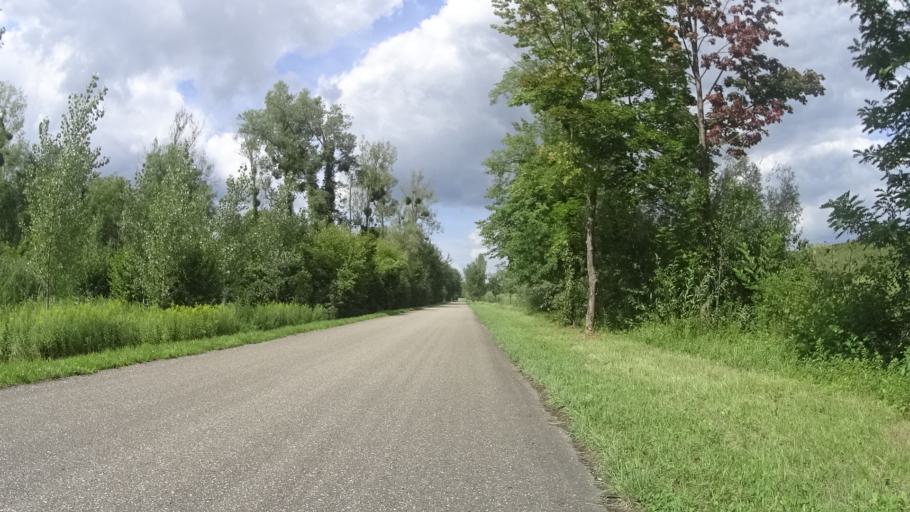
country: DE
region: Baden-Wuerttemberg
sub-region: Karlsruhe Region
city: Rheinmuenster
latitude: 48.7766
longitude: 8.0224
